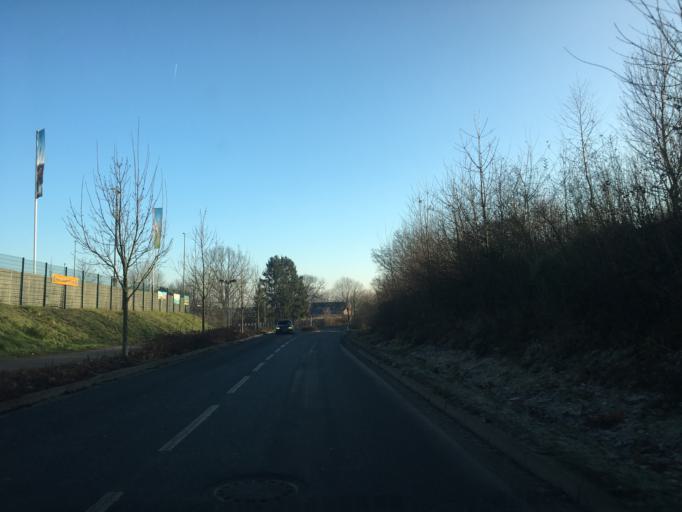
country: DE
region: North Rhine-Westphalia
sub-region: Regierungsbezirk Munster
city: Altenberge
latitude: 52.0486
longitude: 7.4828
